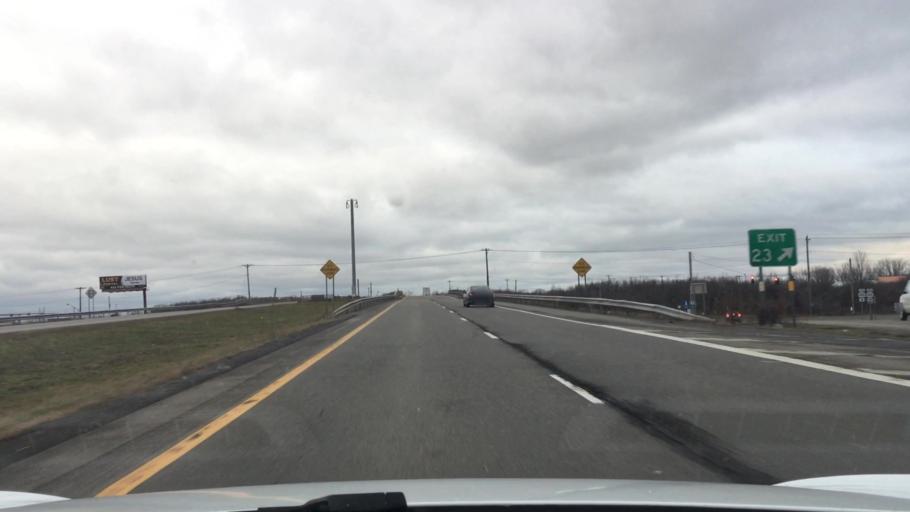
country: US
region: New York
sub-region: Niagara County
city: Niagara Falls
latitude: 43.1065
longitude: -78.9875
